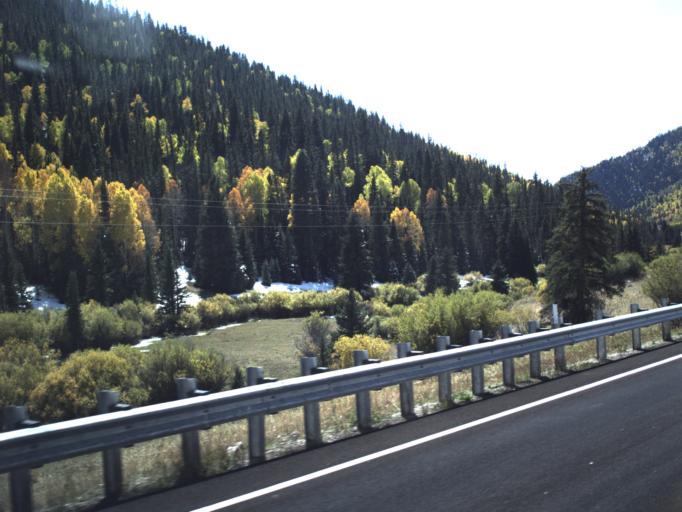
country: US
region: Utah
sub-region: Beaver County
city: Beaver
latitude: 38.3032
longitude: -112.4267
